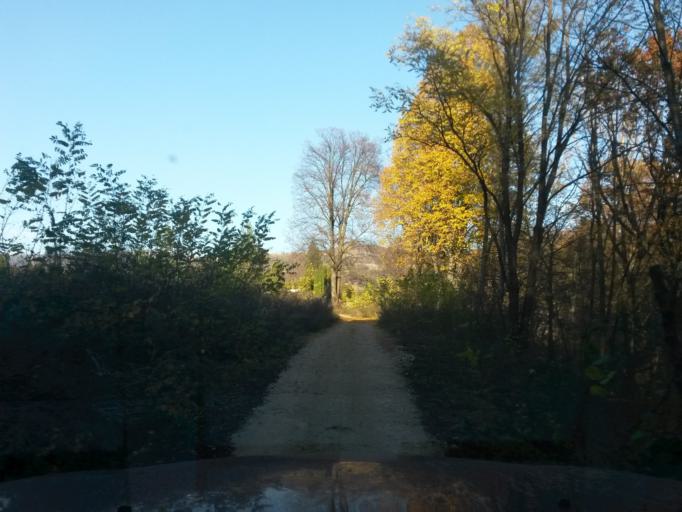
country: SK
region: Kosicky
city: Roznava
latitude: 48.7002
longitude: 20.5143
